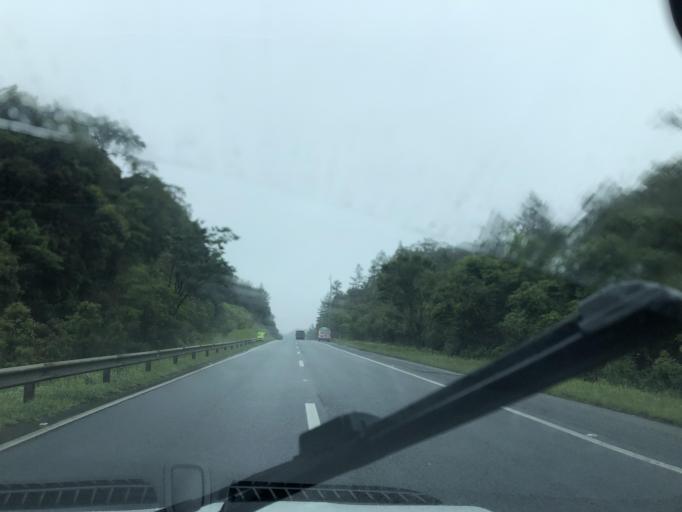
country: BR
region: Parana
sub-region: Antonina
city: Antonina
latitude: -25.1074
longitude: -48.7812
